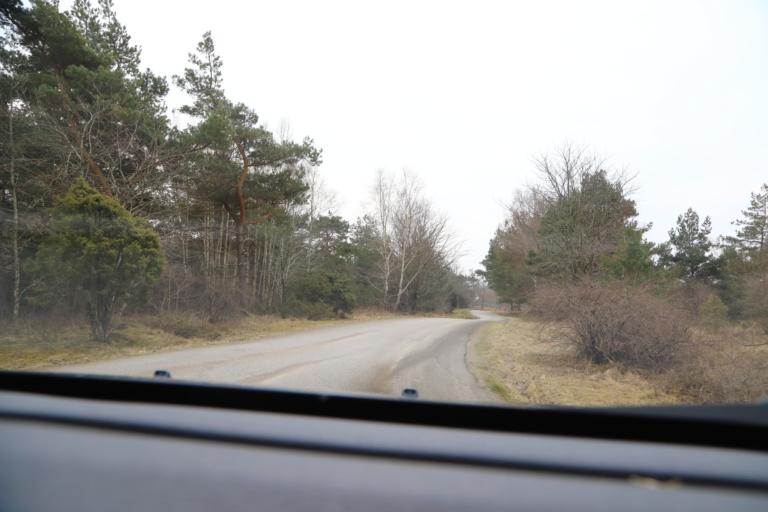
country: SE
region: Halland
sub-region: Kungsbacka Kommun
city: Frillesas
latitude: 57.2634
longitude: 12.1212
